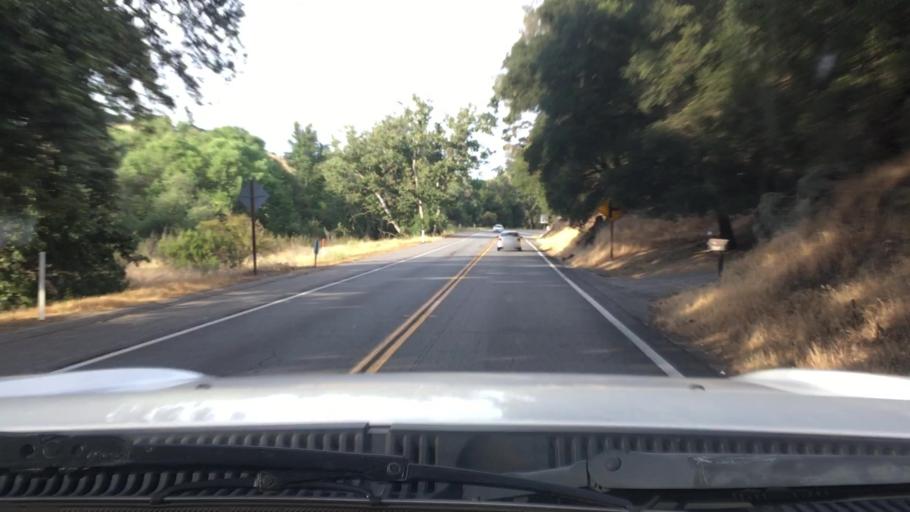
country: US
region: California
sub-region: San Luis Obispo County
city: Atascadero
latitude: 35.4601
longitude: -120.6793
